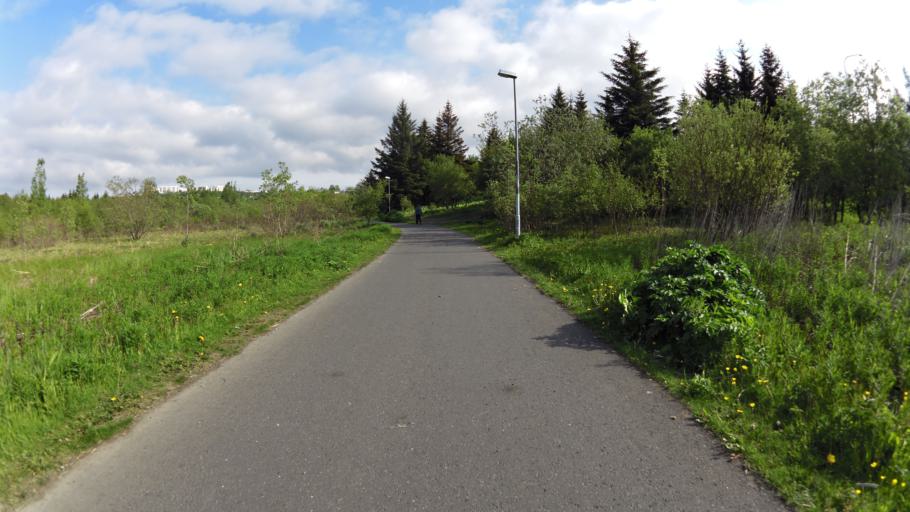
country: IS
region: Capital Region
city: Reykjavik
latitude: 64.1180
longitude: -21.8439
